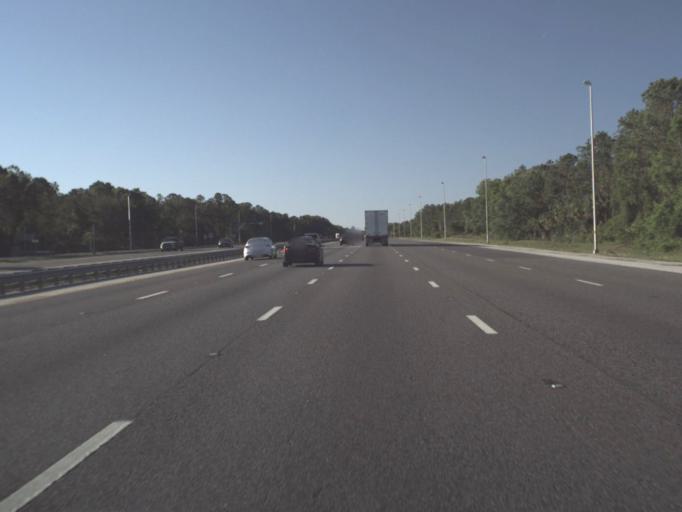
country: US
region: Florida
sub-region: Flagler County
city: Palm Coast
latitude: 29.5147
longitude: -81.1984
